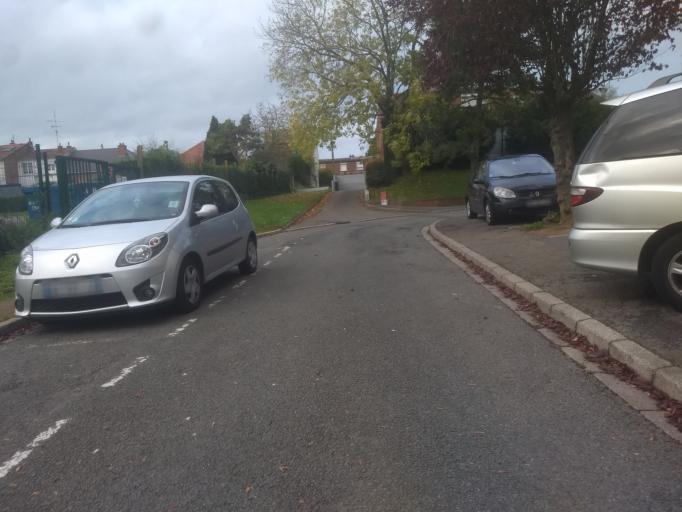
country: FR
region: Nord-Pas-de-Calais
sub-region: Departement du Pas-de-Calais
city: Achicourt
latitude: 50.2920
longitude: 2.7465
